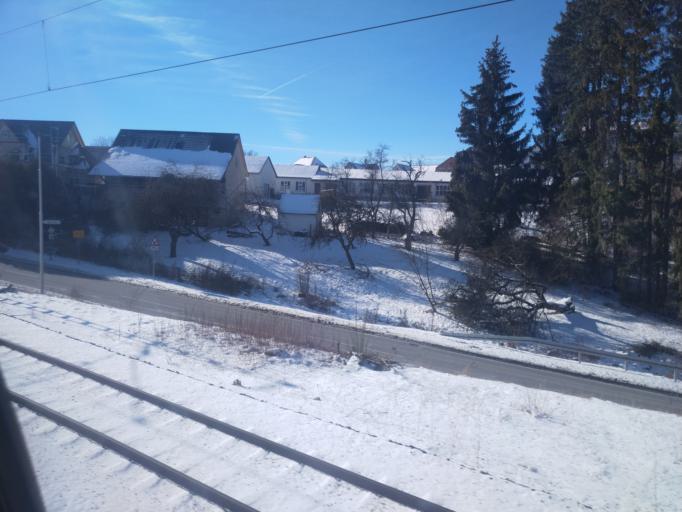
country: DE
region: Baden-Wuerttemberg
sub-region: Freiburg Region
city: Aldingen
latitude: 48.0978
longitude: 8.7120
